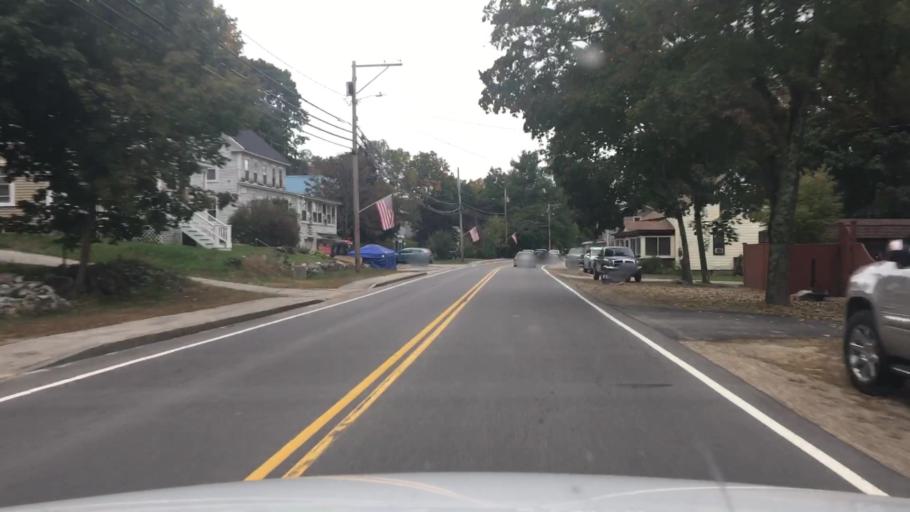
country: US
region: New Hampshire
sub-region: Strafford County
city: New Durham
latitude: 43.4592
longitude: -71.2244
